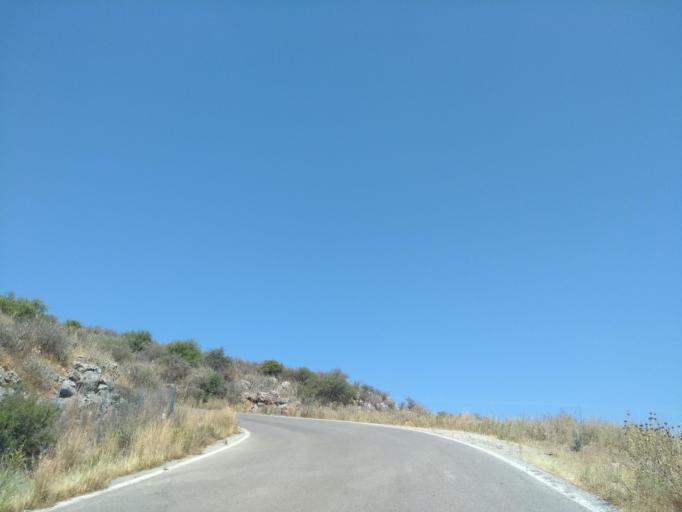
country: GR
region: Crete
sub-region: Nomos Chanias
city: Georgioupolis
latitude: 35.3838
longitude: 24.2361
